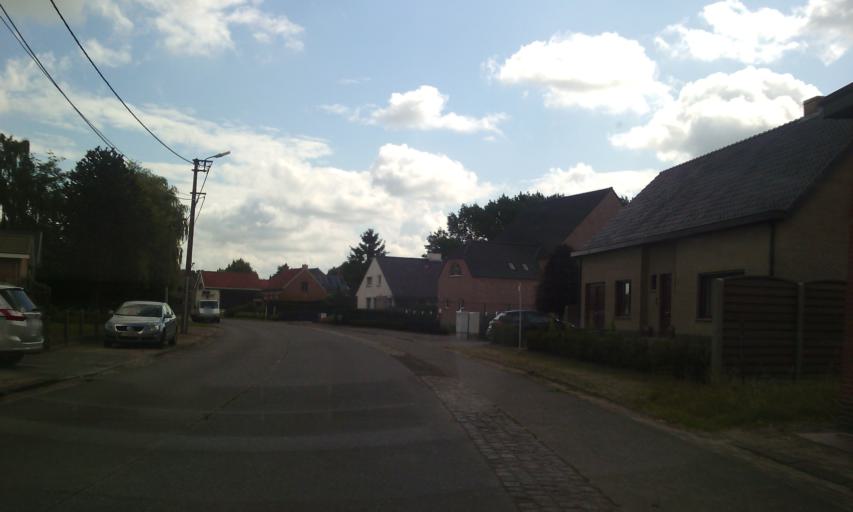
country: BE
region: Flanders
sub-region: Provincie Oost-Vlaanderen
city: Moerbeke
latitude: 51.1488
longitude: 3.9698
